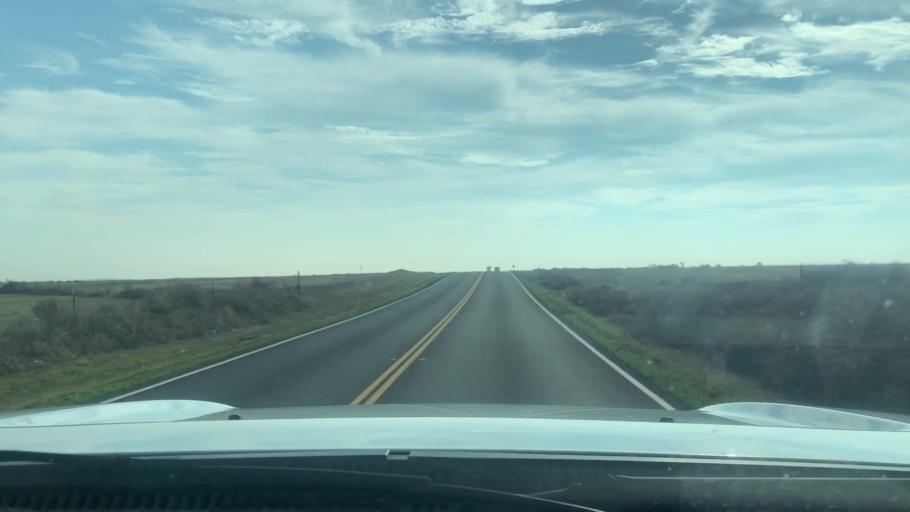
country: US
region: California
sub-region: Kern County
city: Lost Hills
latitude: 35.5860
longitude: -119.8321
